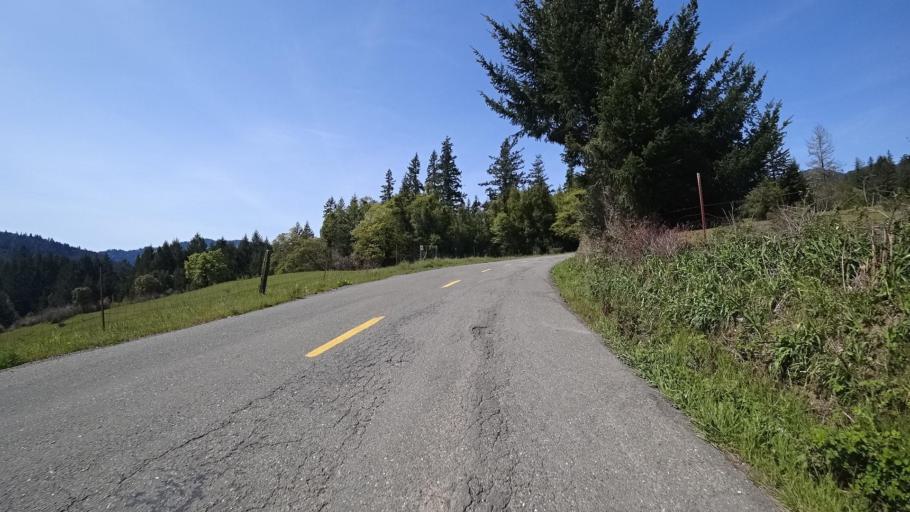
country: US
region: California
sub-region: Humboldt County
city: Redway
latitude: 40.3920
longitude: -123.7470
